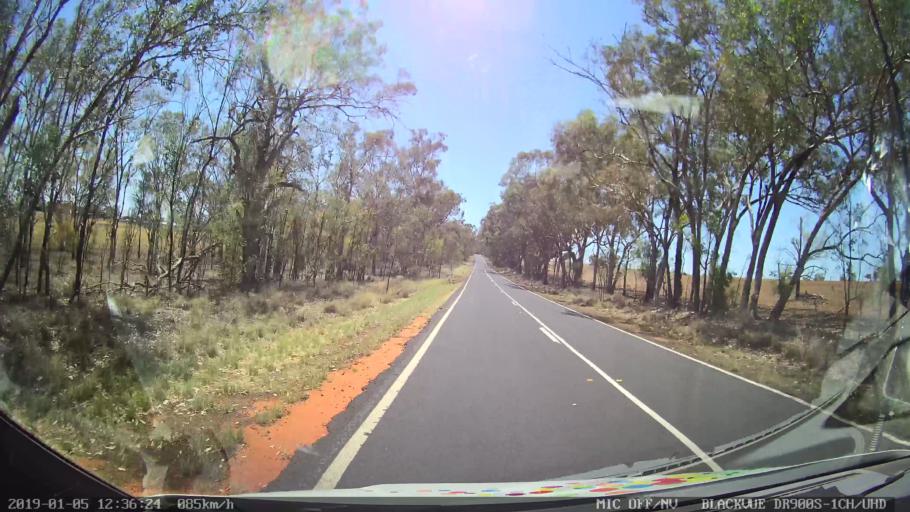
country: AU
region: New South Wales
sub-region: Warrumbungle Shire
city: Coonabarabran
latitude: -31.2073
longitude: 149.4397
